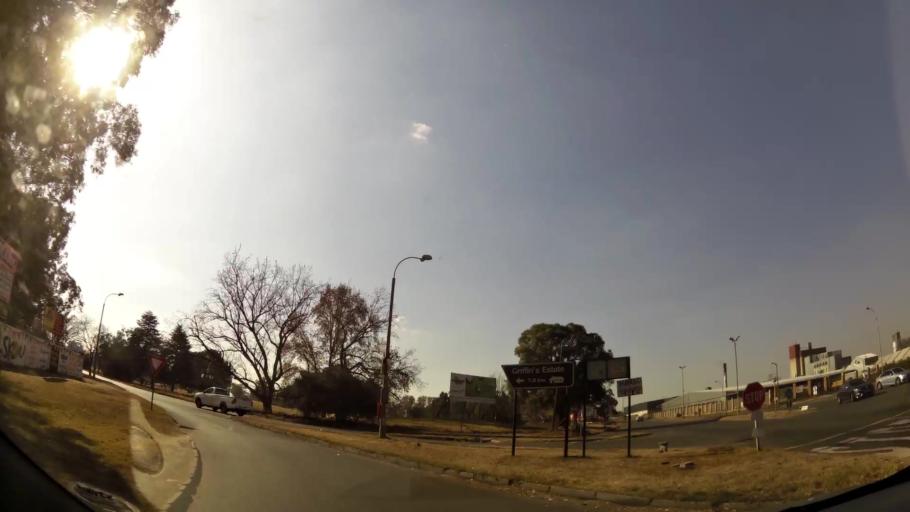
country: ZA
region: Gauteng
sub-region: West Rand District Municipality
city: Randfontein
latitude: -26.1649
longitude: 27.7077
